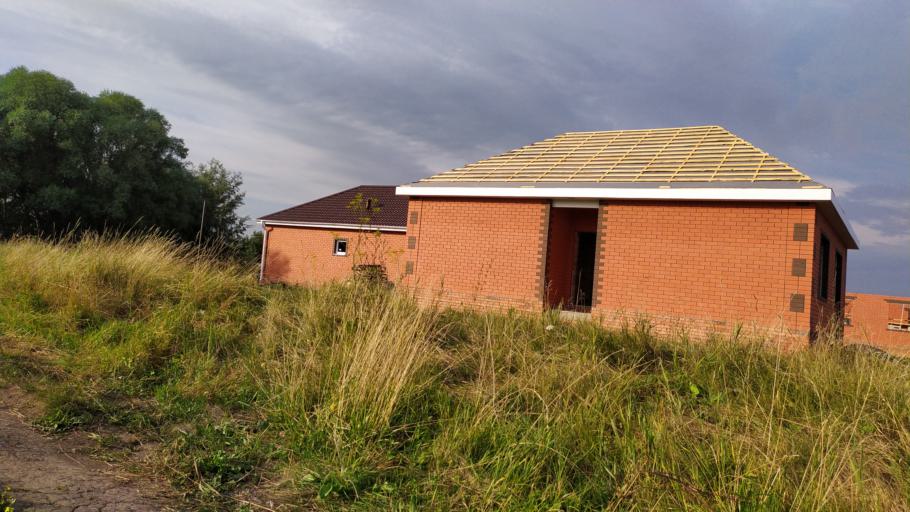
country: RU
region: Kursk
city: Kursk
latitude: 51.6423
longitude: 36.1573
